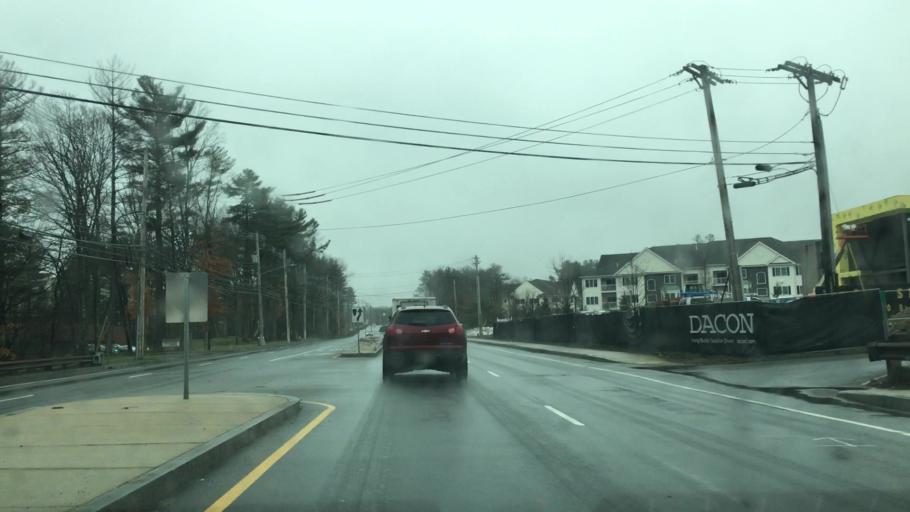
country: US
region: Massachusetts
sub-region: Middlesex County
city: Pinehurst
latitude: 42.5127
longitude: -71.2389
